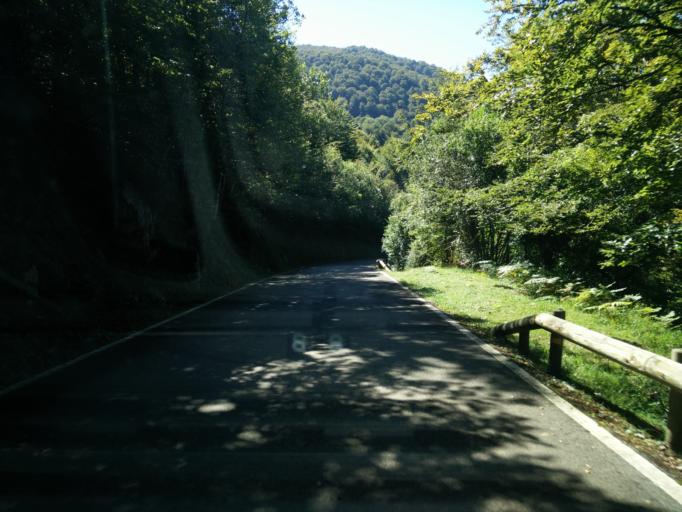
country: ES
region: Cantabria
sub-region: Provincia de Cantabria
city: Ruente
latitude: 43.1130
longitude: -4.2860
